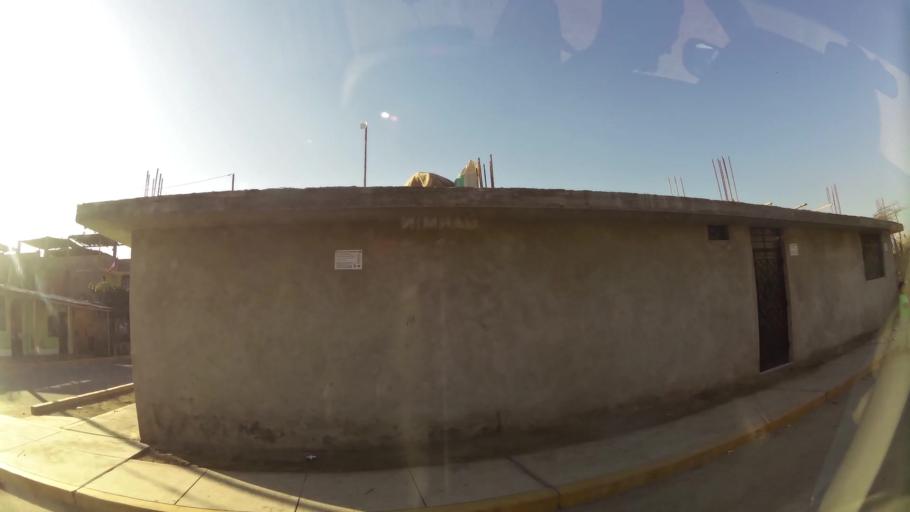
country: PE
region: Ica
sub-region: Provincia de Ica
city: Ica
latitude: -14.0682
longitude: -75.7168
